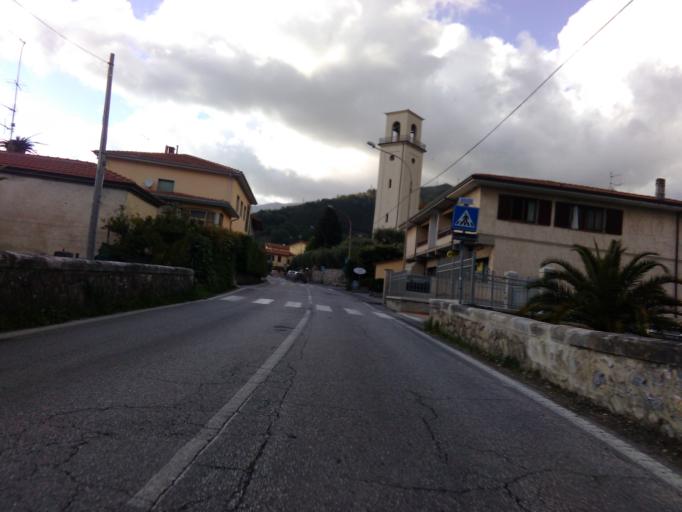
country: IT
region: Tuscany
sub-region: Provincia di Lucca
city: Seravezza
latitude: 43.9807
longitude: 10.2205
